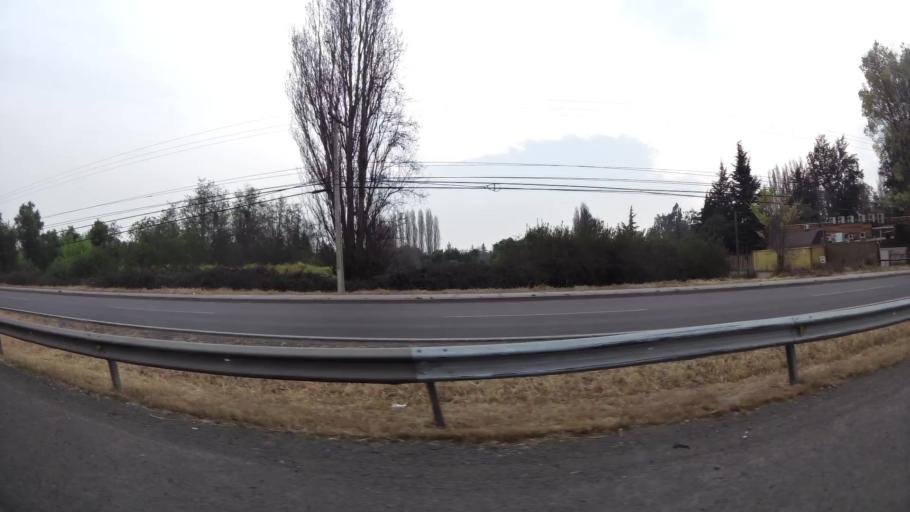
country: CL
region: Santiago Metropolitan
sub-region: Provincia de Chacabuco
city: Chicureo Abajo
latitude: -33.2675
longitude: -70.6999
